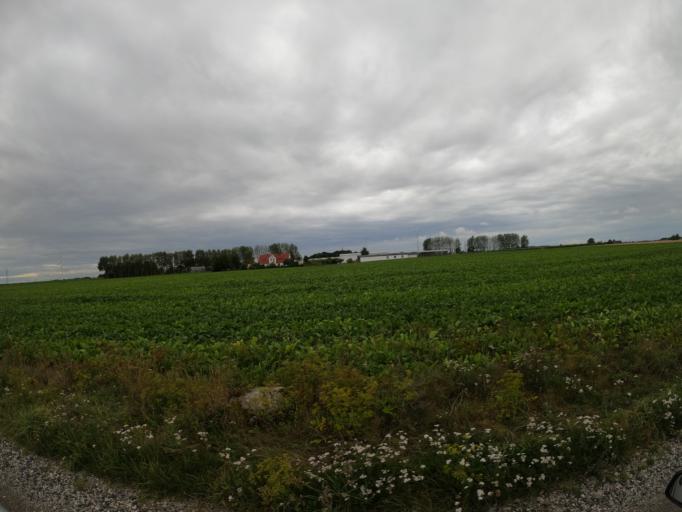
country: SE
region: Skane
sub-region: Kavlinge Kommun
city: Kaevlinge
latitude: 55.7493
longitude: 13.1292
